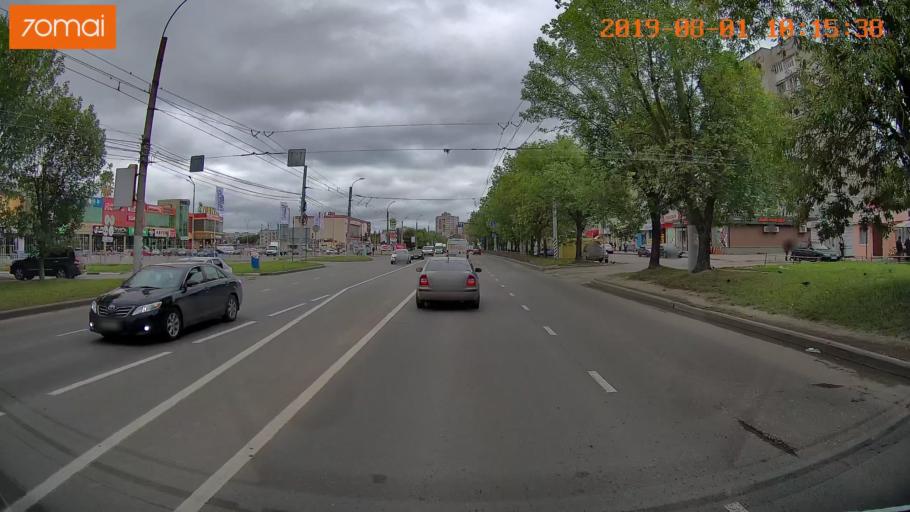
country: RU
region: Ivanovo
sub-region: Gorod Ivanovo
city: Ivanovo
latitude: 56.9637
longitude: 40.9877
